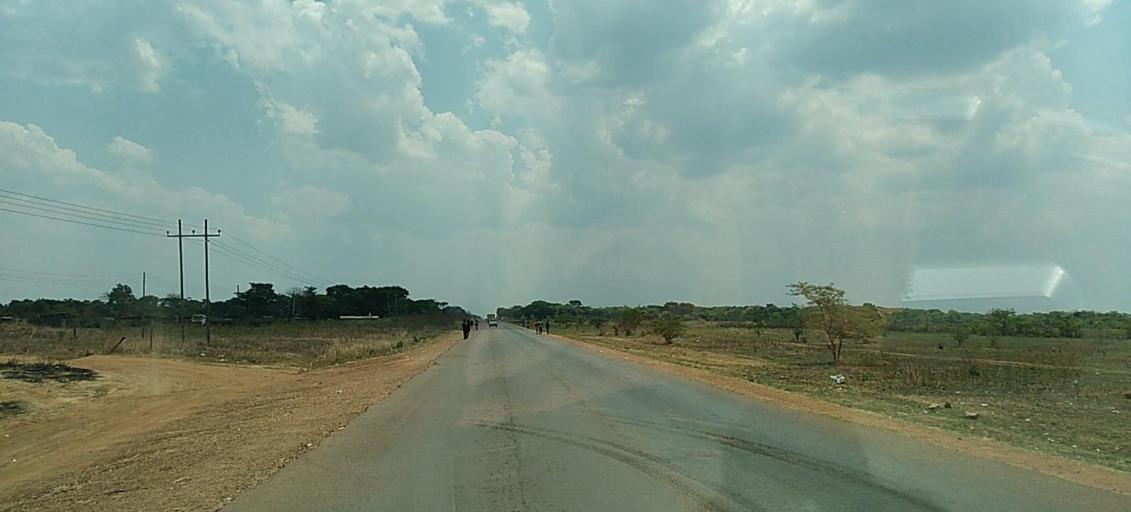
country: ZM
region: Copperbelt
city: Kalulushi
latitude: -12.8345
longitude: 27.9657
